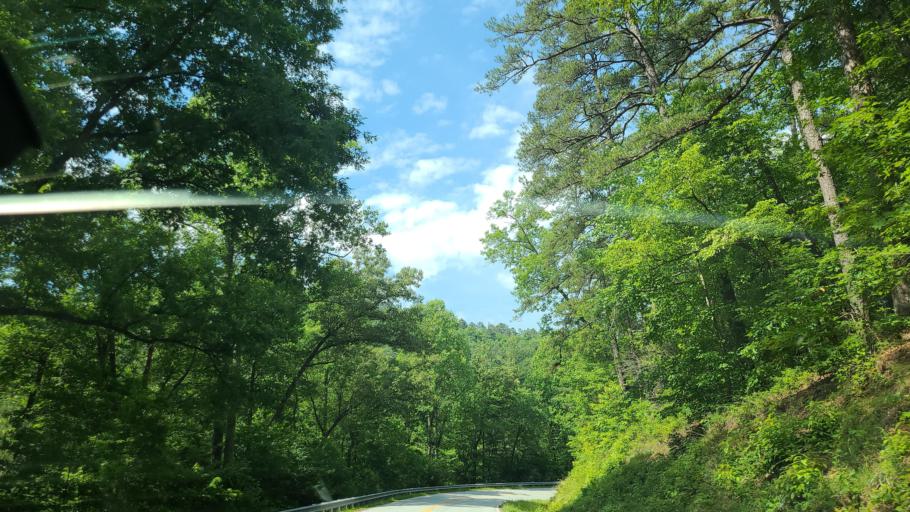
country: US
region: South Carolina
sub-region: Oconee County
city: Walhalla
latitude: 34.8985
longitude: -83.1784
